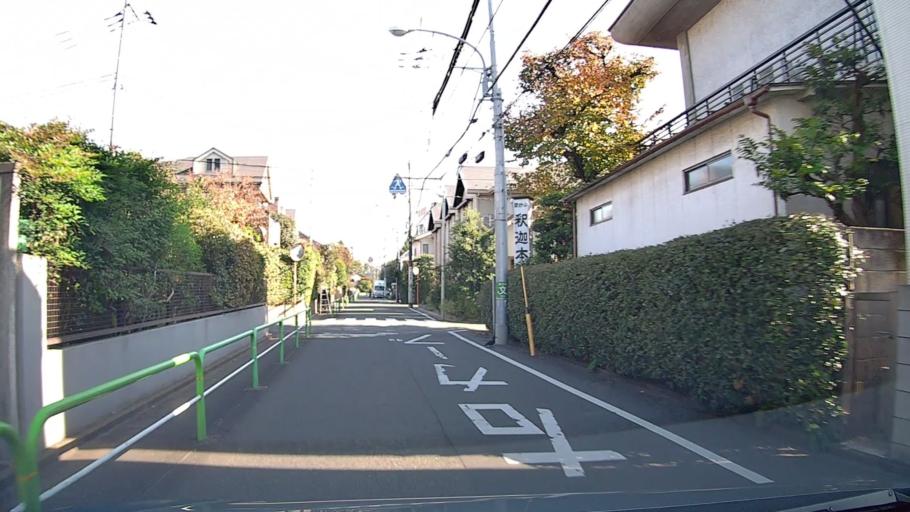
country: JP
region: Tokyo
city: Musashino
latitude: 35.7354
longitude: 139.5940
